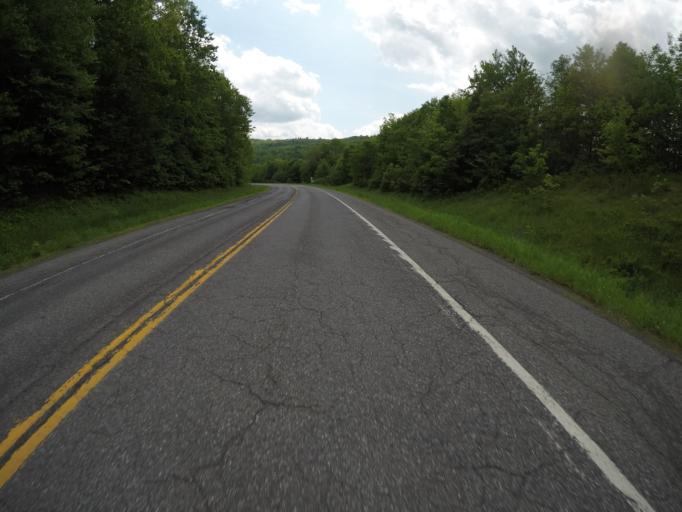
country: US
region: New York
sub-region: Delaware County
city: Stamford
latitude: 42.2081
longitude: -74.5989
